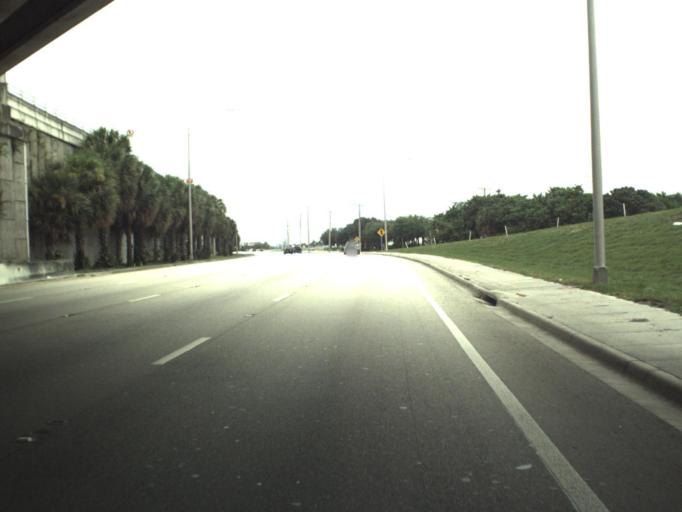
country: US
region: Florida
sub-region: Palm Beach County
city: Lake Clarke Shores
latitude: 26.6771
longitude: -80.0820
